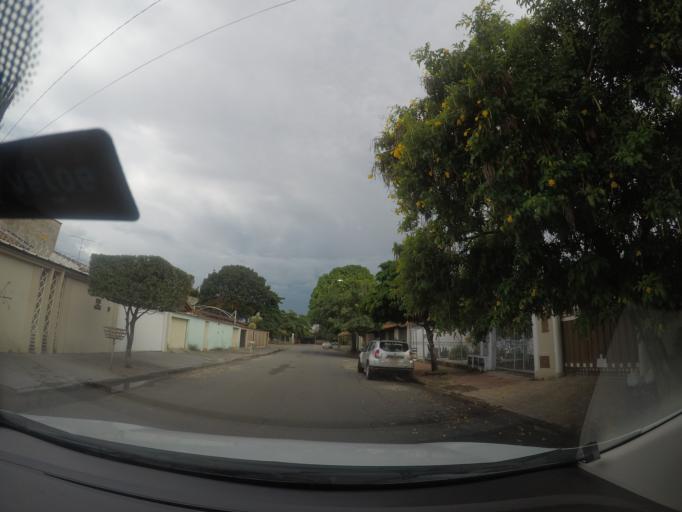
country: BR
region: Goias
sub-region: Goiania
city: Goiania
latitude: -16.6681
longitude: -49.2793
